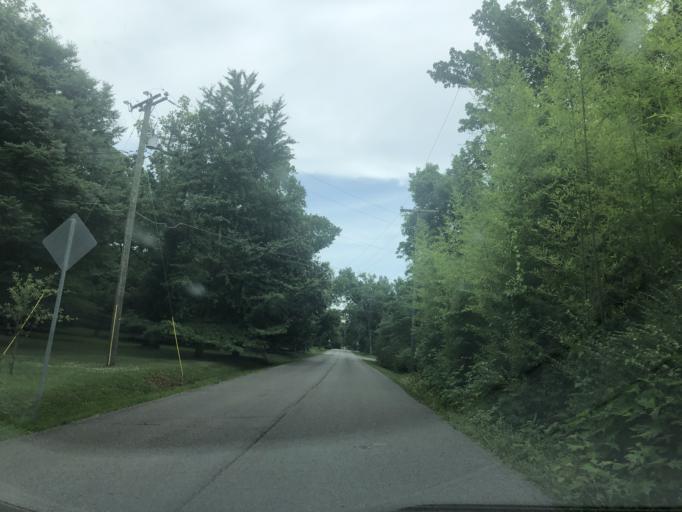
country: US
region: Tennessee
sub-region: Davidson County
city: Oak Hill
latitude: 36.1009
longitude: -86.7772
